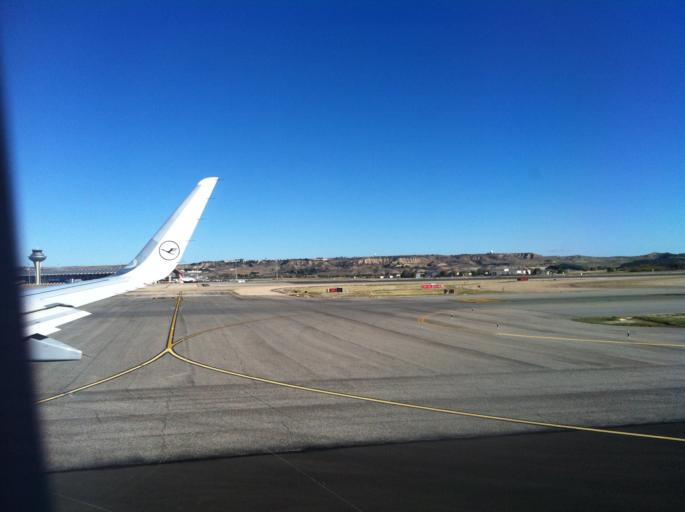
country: ES
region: Madrid
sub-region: Provincia de Madrid
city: Barajas de Madrid
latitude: 40.4835
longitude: -3.5784
